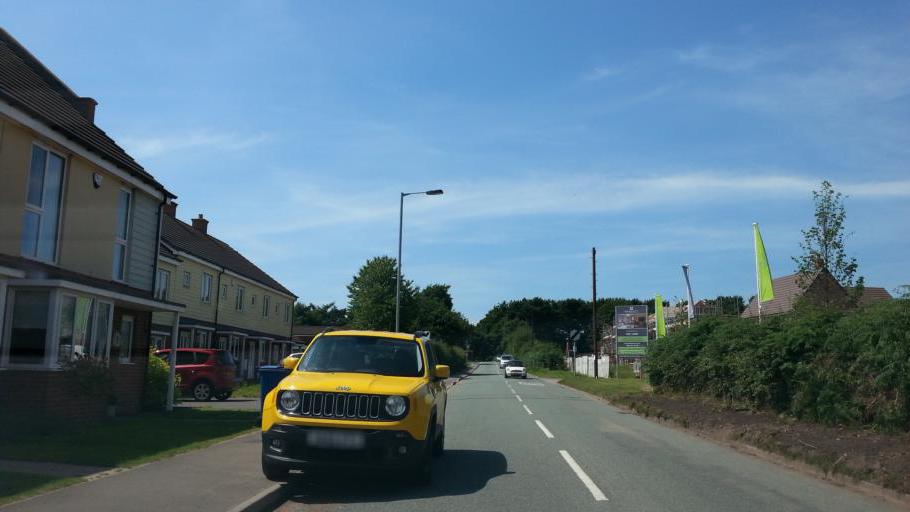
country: GB
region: England
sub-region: Staffordshire
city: Cannock
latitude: 52.7133
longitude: -2.0273
